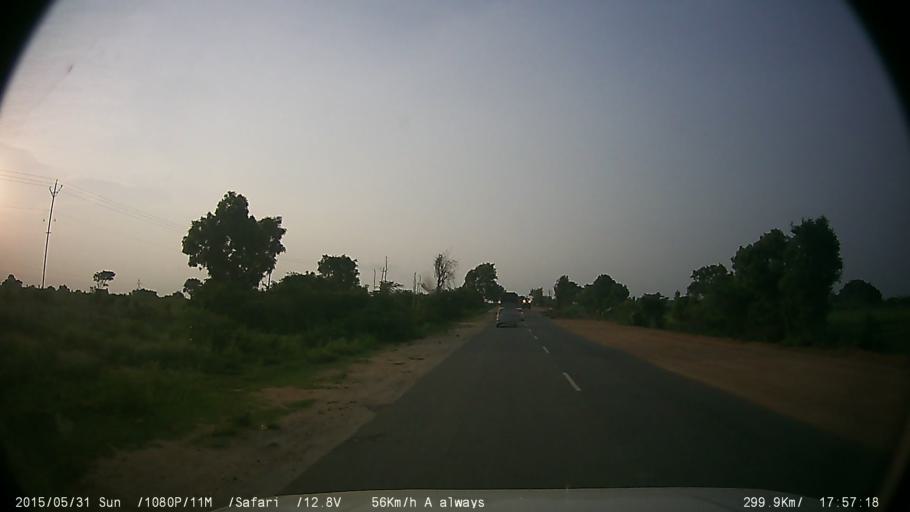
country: IN
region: Karnataka
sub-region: Mysore
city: Nanjangud
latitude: 12.0002
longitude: 76.6693
